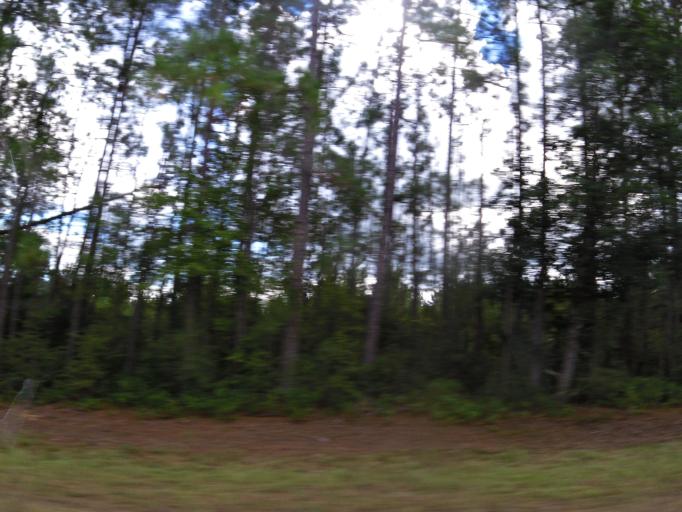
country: US
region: Georgia
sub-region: Brantley County
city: Nahunta
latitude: 31.0261
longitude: -82.0228
